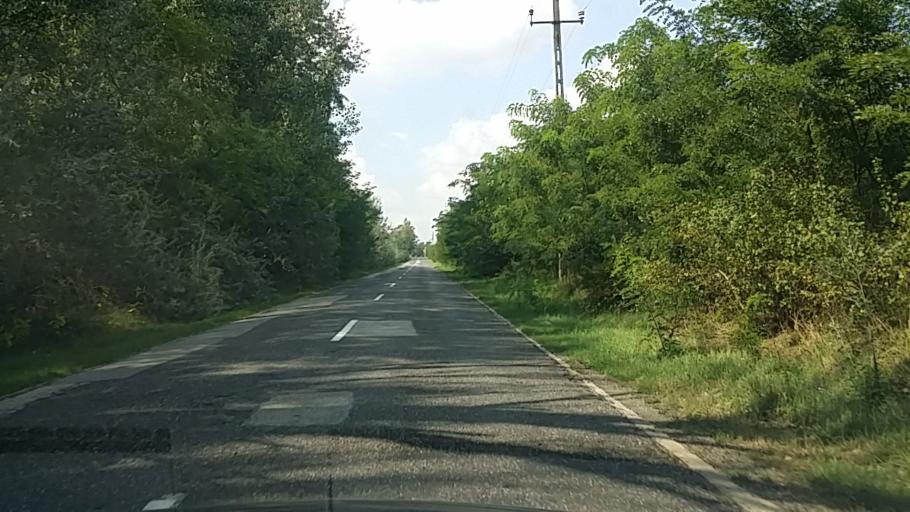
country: HU
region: Bacs-Kiskun
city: Lakitelek
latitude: 46.8628
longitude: 19.9692
